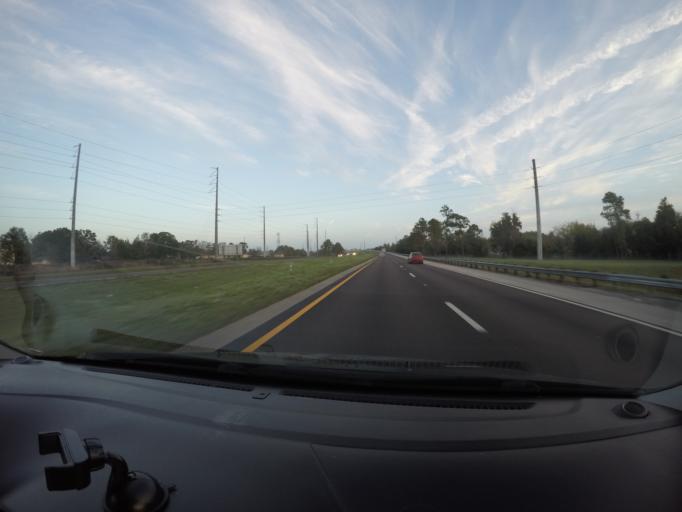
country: US
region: Florida
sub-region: Orange County
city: Union Park
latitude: 28.5351
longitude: -81.2508
